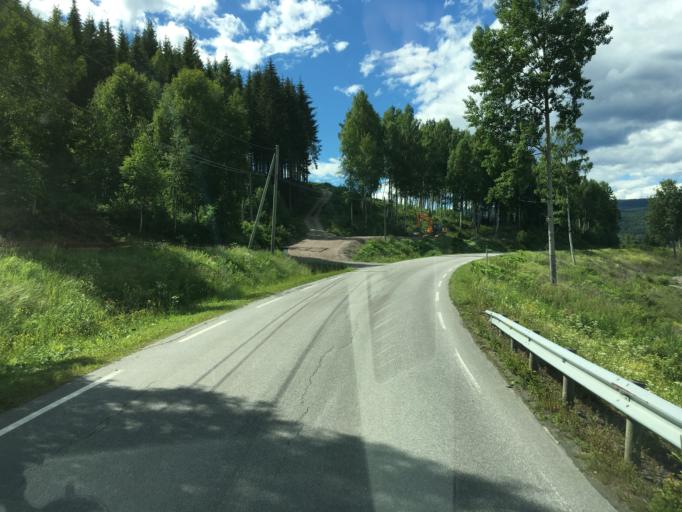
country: NO
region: Oppland
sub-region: Sondre Land
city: Hov
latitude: 60.5114
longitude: 10.3193
